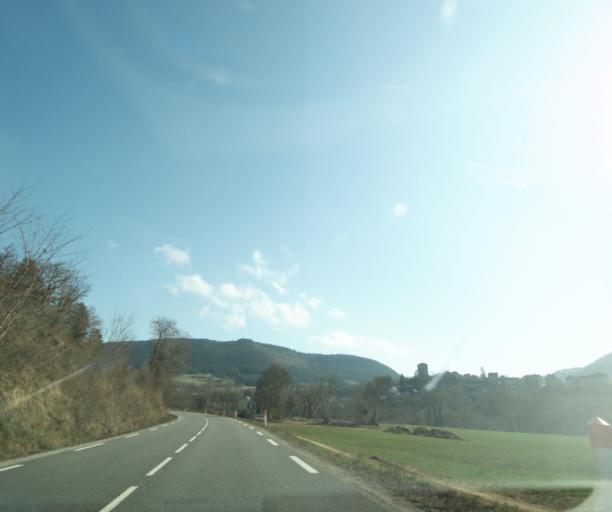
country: FR
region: Languedoc-Roussillon
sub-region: Departement de la Lozere
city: Chanac
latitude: 44.4705
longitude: 3.3383
